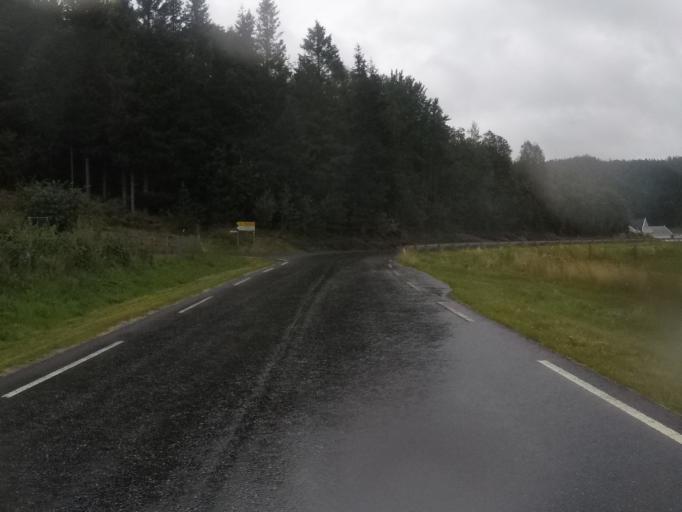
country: NO
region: Vest-Agder
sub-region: Audnedal
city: Konsmo
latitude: 58.2790
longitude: 7.2867
